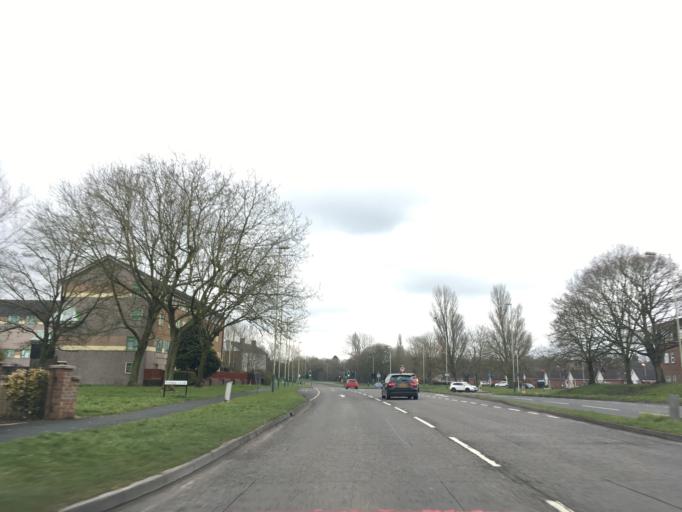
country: GB
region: England
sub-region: Borough of Swindon
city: Swindon
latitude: 51.5516
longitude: -1.7584
